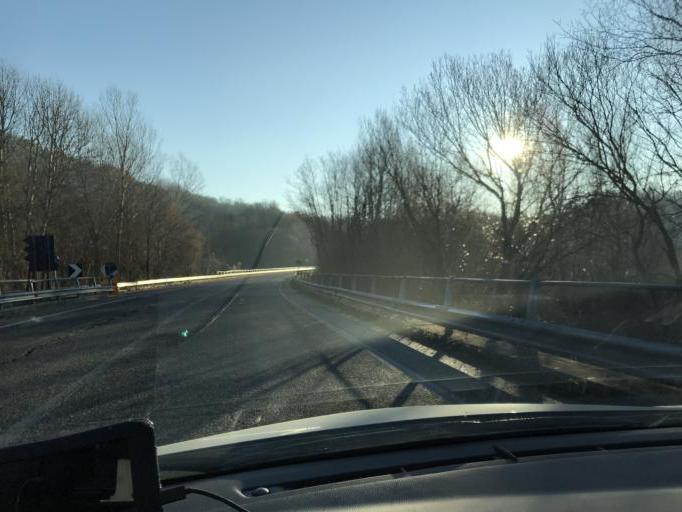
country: IT
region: Latium
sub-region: Provincia di Rieti
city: Fiamignano
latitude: 42.2641
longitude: 13.1063
